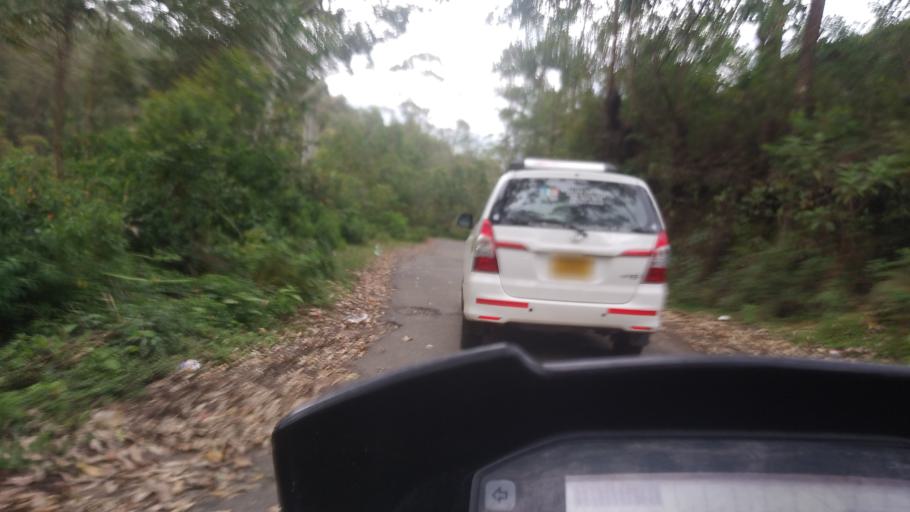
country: IN
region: Kerala
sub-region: Idukki
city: Munnar
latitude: 10.0607
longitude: 77.1072
